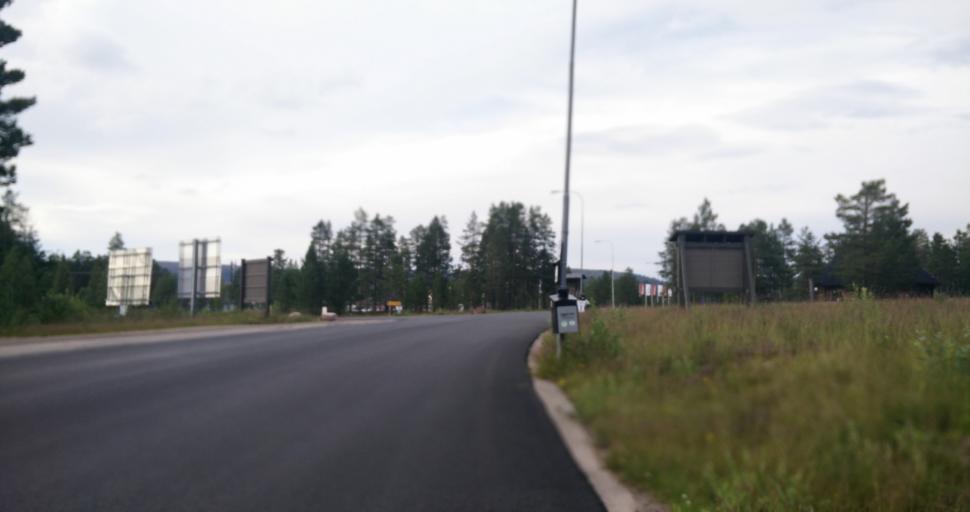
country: NO
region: Hedmark
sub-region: Trysil
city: Innbygda
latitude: 61.1771
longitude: 12.9922
